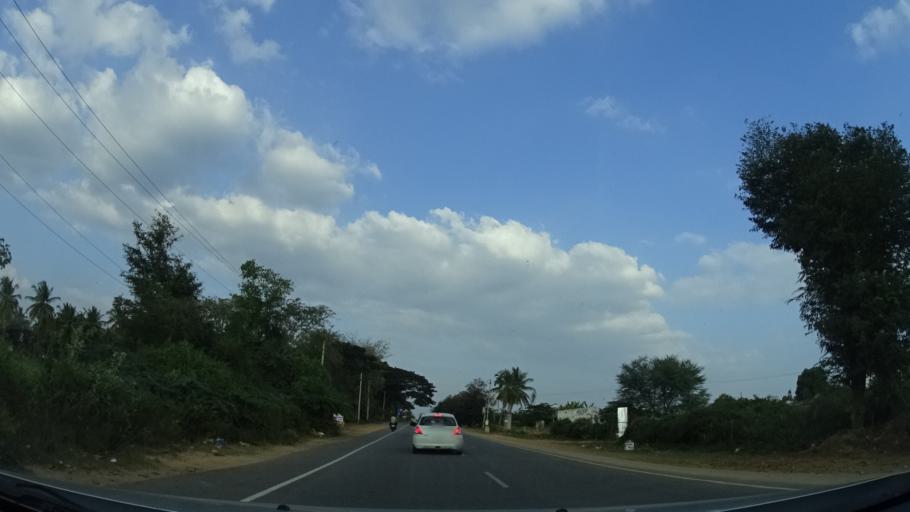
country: IN
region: Karnataka
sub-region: Mandya
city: Malavalli
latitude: 12.3784
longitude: 77.0410
